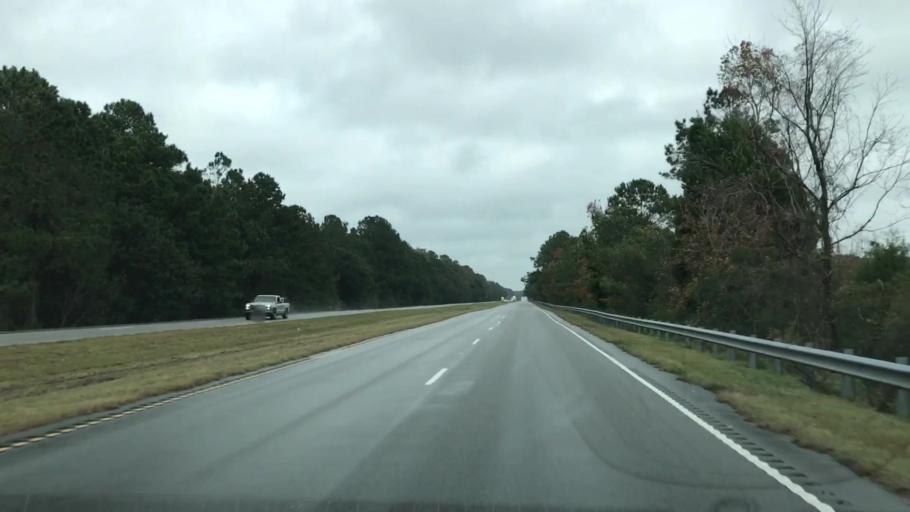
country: US
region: South Carolina
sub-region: Georgetown County
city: Georgetown
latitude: 33.1967
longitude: -79.3947
